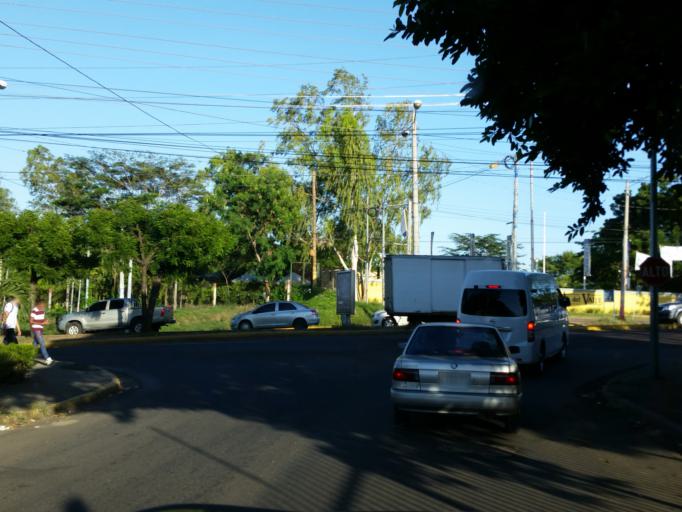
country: NI
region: Managua
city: Managua
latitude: 12.1247
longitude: -86.2838
